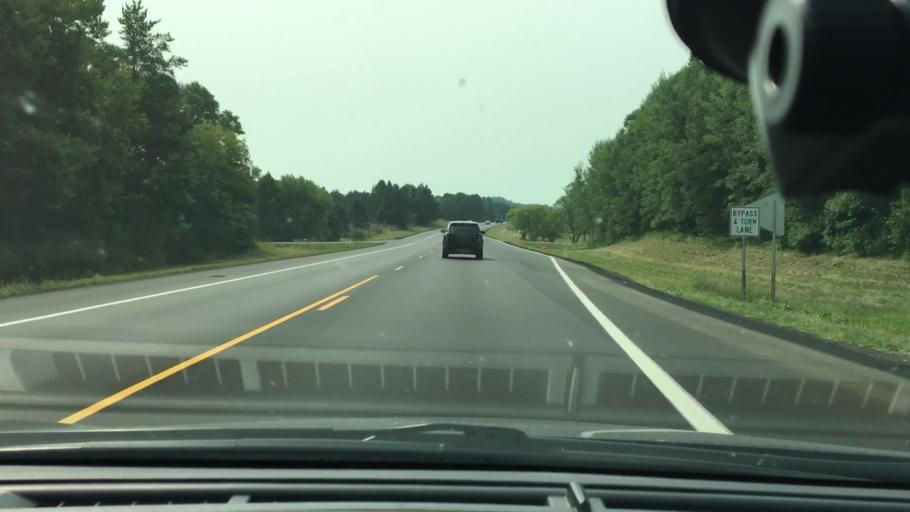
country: US
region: Minnesota
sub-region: Crow Wing County
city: Brainerd
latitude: 46.4070
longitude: -94.1760
